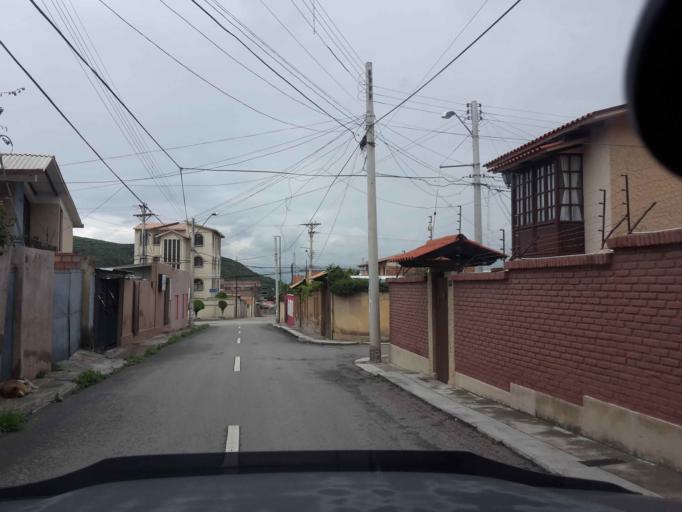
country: BO
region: Cochabamba
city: Cochabamba
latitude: -17.3756
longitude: -66.1229
